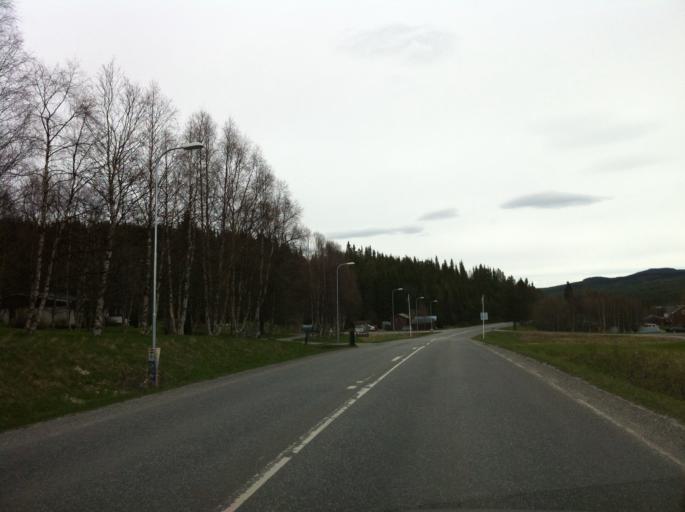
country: NO
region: Hedmark
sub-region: Engerdal
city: Engerdal
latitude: 62.5402
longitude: 12.5505
